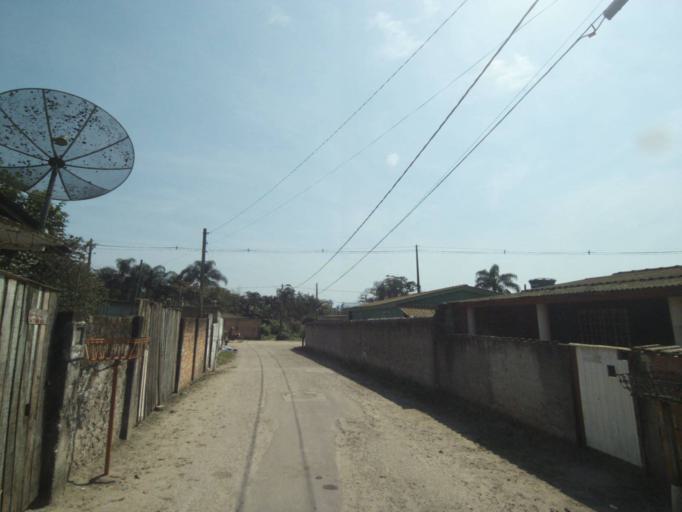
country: BR
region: Parana
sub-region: Paranagua
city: Paranagua
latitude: -25.5510
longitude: -48.5602
